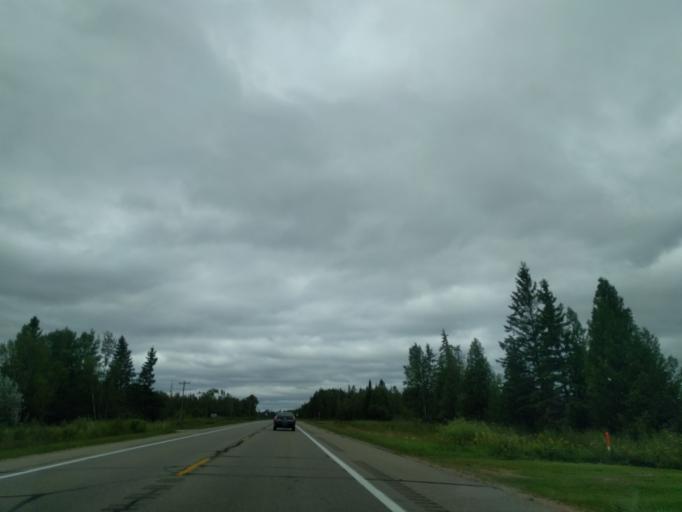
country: US
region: Michigan
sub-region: Delta County
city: Escanaba
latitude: 45.6375
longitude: -87.1990
